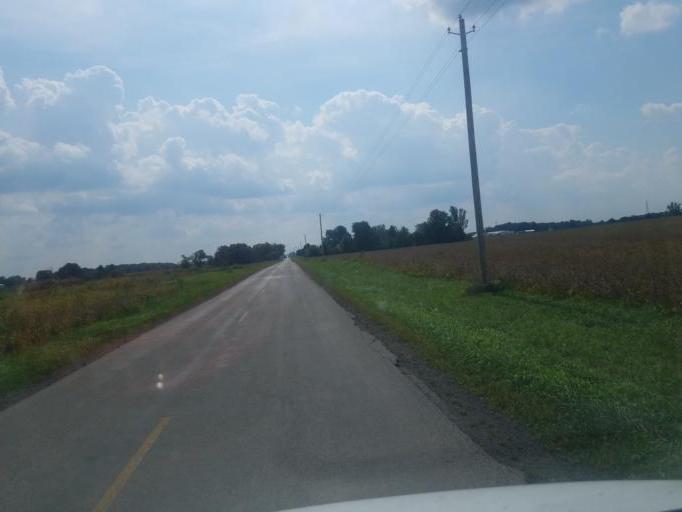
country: US
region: Ohio
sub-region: Hardin County
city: Ada
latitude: 40.6282
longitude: -83.7637
